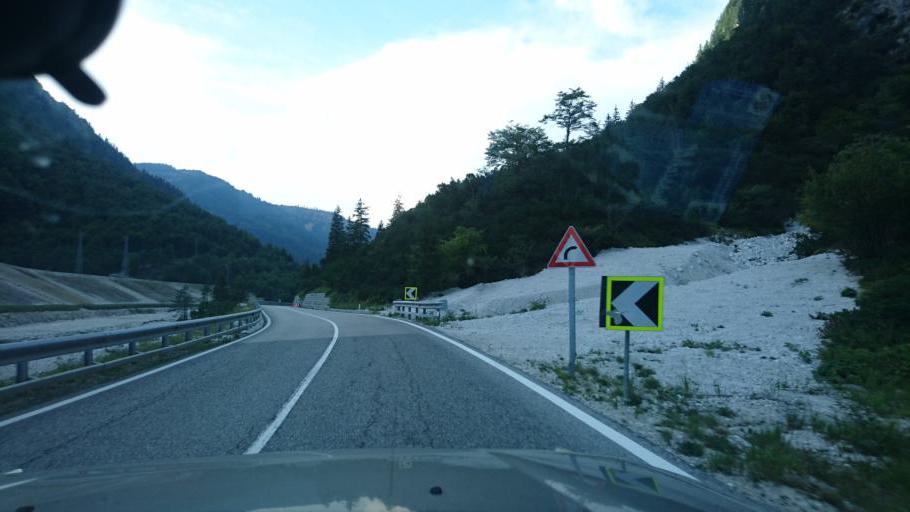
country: IT
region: Friuli Venezia Giulia
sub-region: Provincia di Udine
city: Tarvisio
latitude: 46.4561
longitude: 13.5752
